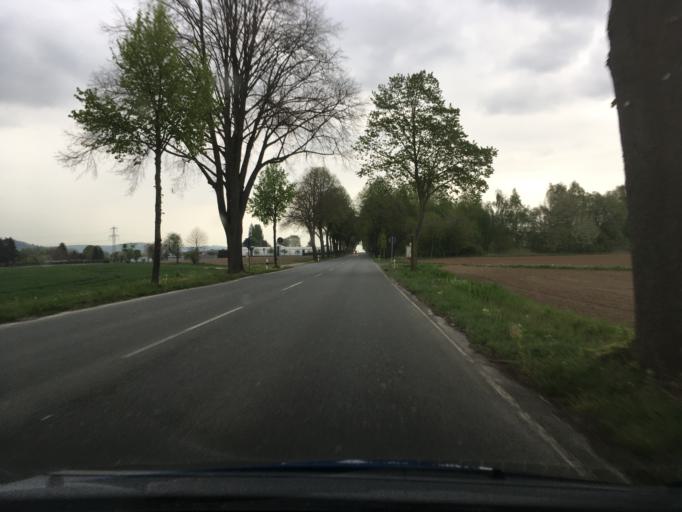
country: DE
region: Lower Saxony
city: Einbeck
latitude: 51.8245
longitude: 9.8444
